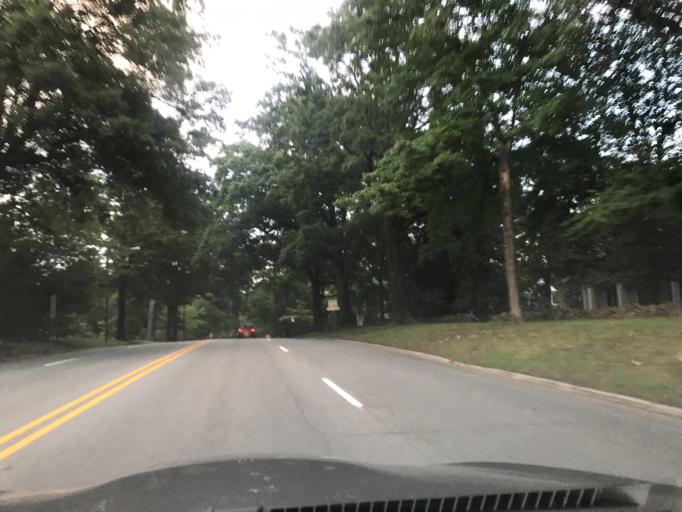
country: US
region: North Carolina
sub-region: Orange County
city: Chapel Hill
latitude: 35.9161
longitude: -79.0481
